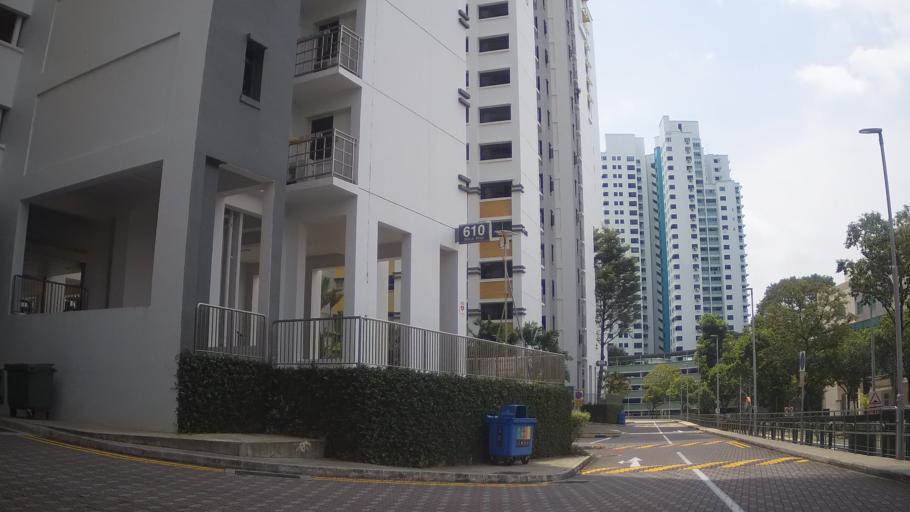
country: MY
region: Johor
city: Johor Bahru
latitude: 1.3834
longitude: 103.7610
